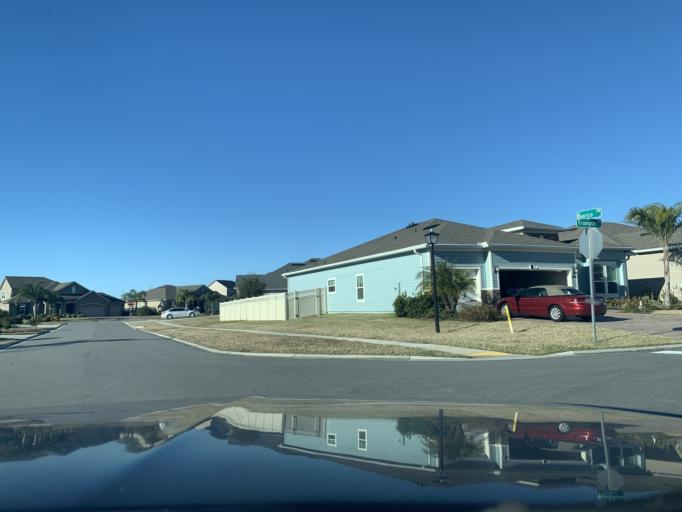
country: US
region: Florida
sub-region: Clay County
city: Green Cove Springs
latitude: 29.9775
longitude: -81.5248
